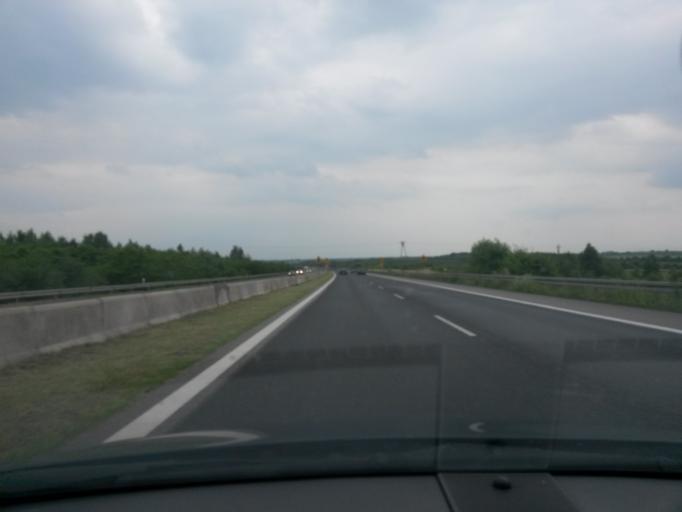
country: PL
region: Silesian Voivodeship
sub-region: Powiat czestochowski
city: Koscielec
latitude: 50.8884
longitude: 19.1758
